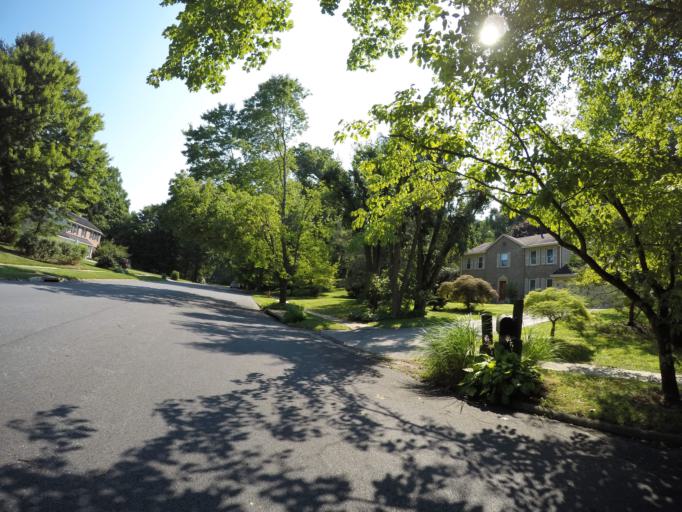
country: US
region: Maryland
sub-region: Howard County
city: Columbia
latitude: 39.2706
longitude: -76.8603
